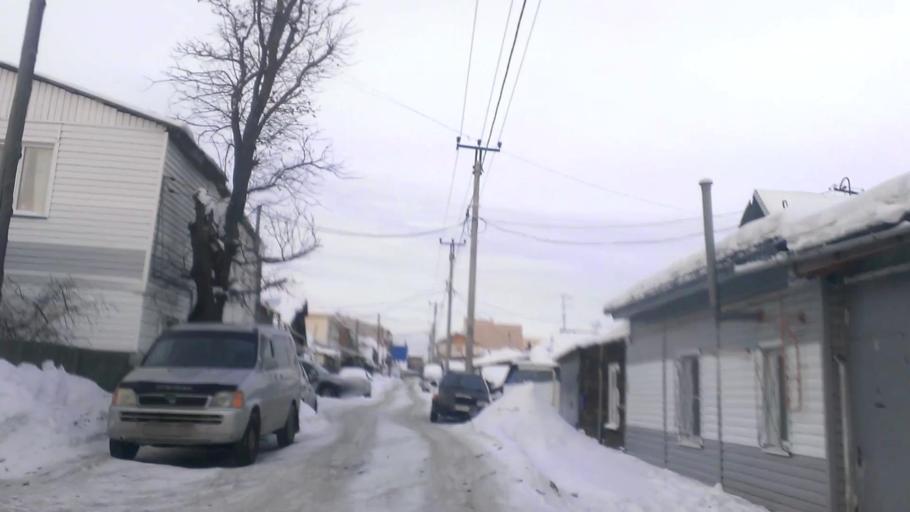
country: RU
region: Altai Krai
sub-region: Gorod Barnaulskiy
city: Barnaul
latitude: 53.3483
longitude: 83.6943
